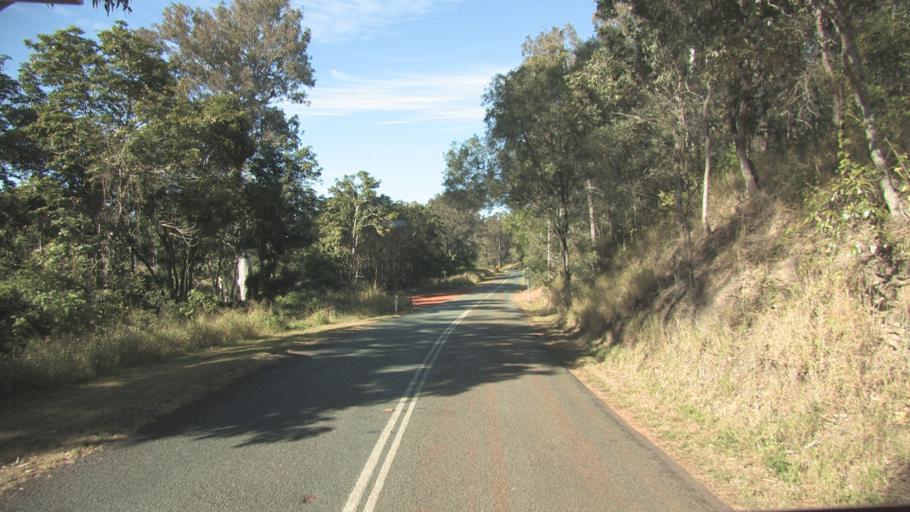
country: AU
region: Queensland
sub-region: Logan
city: Windaroo
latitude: -27.8016
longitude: 153.1684
